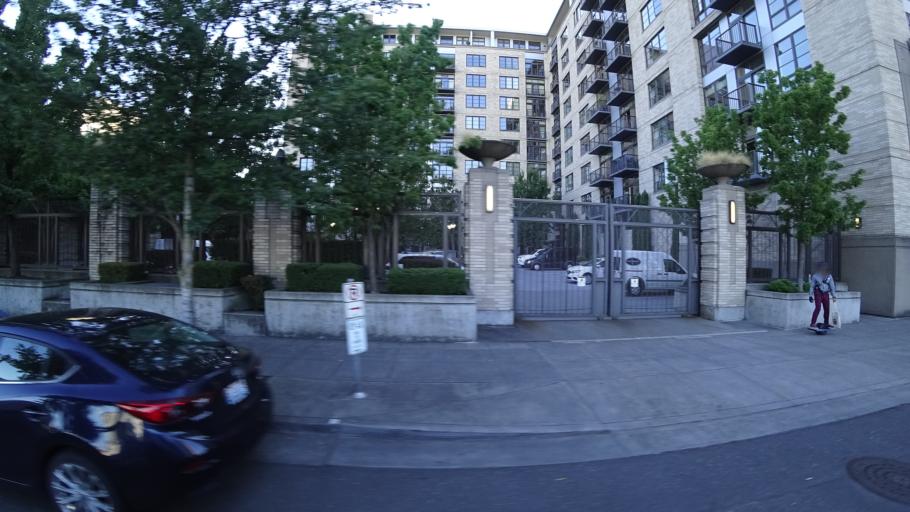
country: US
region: Oregon
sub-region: Multnomah County
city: Portland
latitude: 45.5300
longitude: -122.6804
